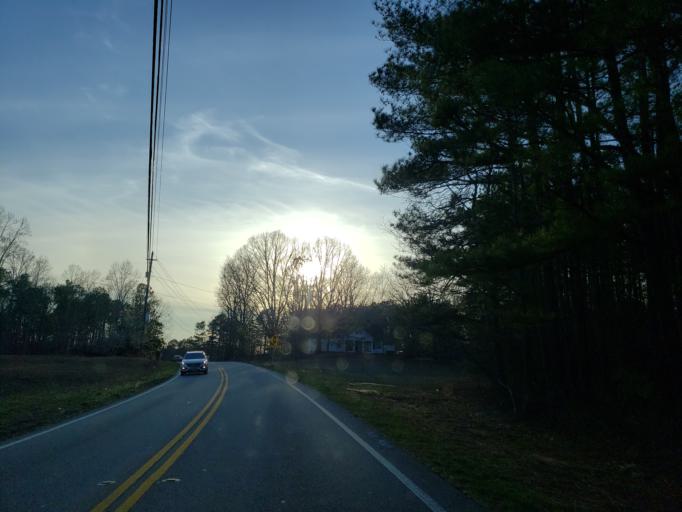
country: US
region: Georgia
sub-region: Cobb County
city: Acworth
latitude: 33.9793
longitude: -84.7371
